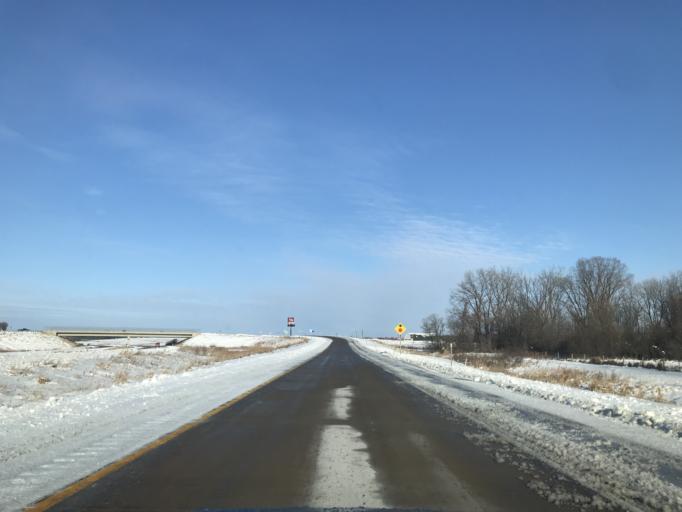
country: US
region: Wisconsin
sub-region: Oconto County
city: Oconto Falls
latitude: 44.9478
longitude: -88.0375
